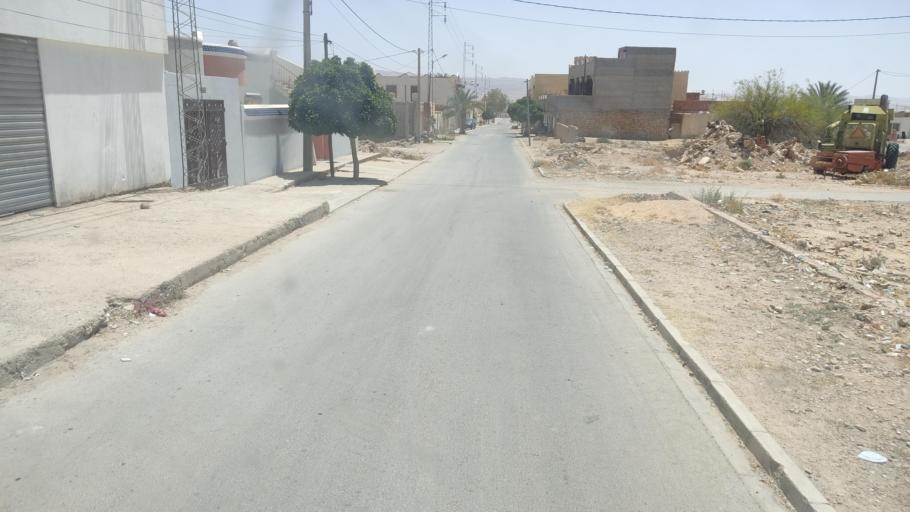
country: TN
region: Gafsa
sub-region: Gafsa Municipality
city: Gafsa
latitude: 34.3398
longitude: 8.9423
